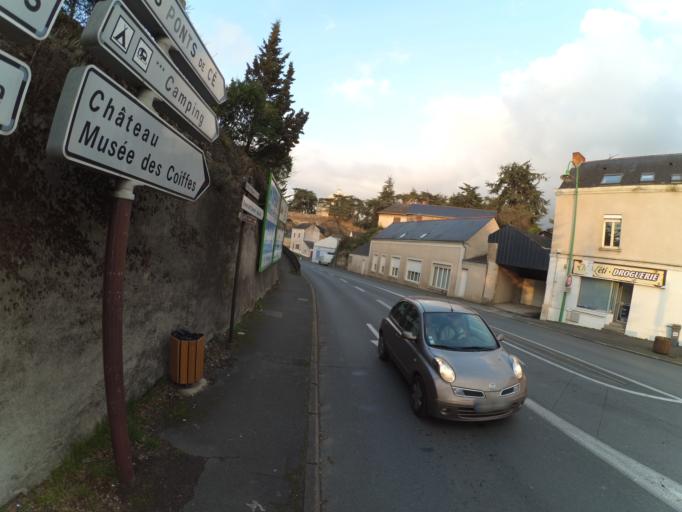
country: FR
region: Pays de la Loire
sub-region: Departement de Maine-et-Loire
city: Les Ponts-de-Ce
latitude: 47.4046
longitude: -0.5261
